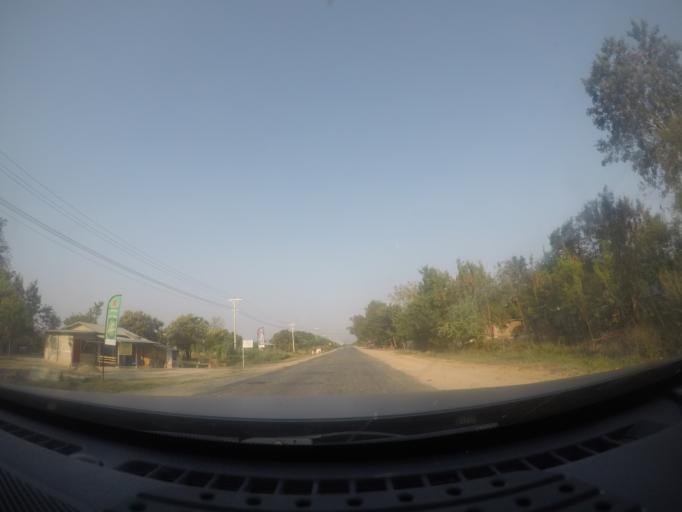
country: MM
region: Mandalay
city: Yamethin
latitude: 20.6489
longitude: 96.1011
